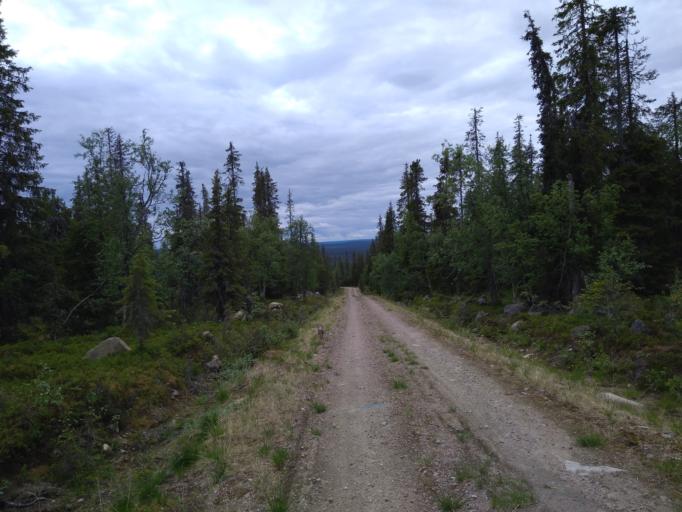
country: FI
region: Lapland
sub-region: Tunturi-Lappi
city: Muonio
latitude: 67.9675
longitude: 24.0865
